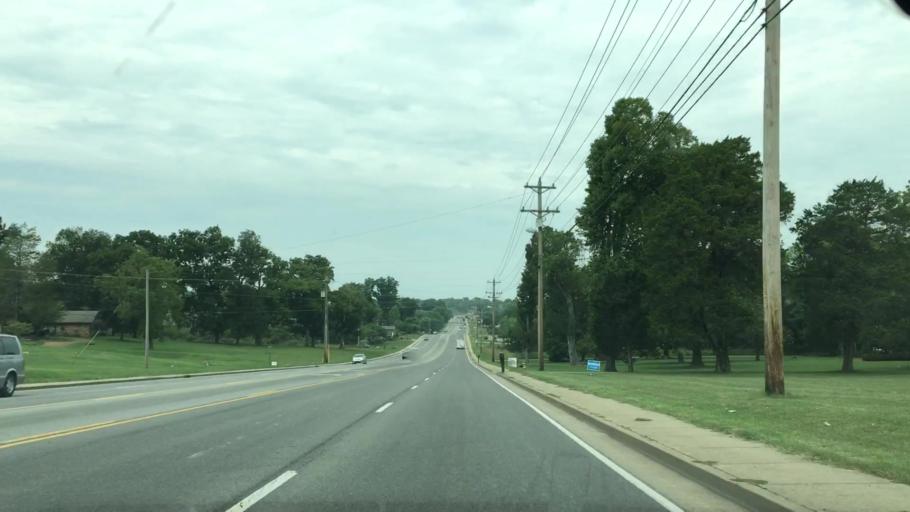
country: US
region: Tennessee
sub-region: Wilson County
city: Lebanon
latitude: 36.2241
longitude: -86.3519
